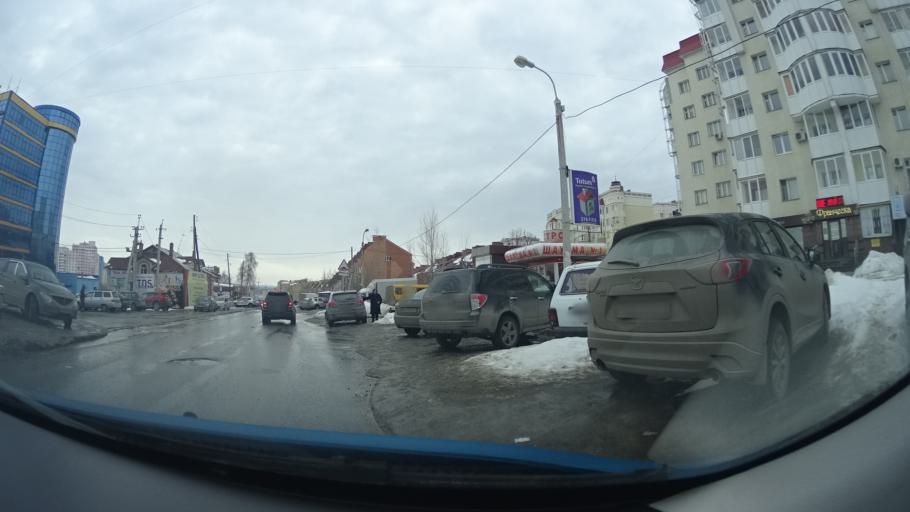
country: RU
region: Bashkortostan
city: Ufa
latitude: 54.6972
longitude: 55.9905
